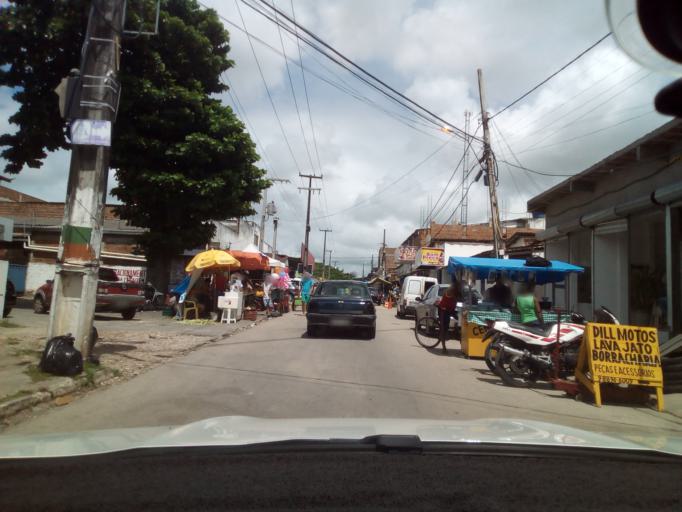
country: BR
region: Paraiba
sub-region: Bayeux
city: Bayeux
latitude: -7.1473
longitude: -34.9245
